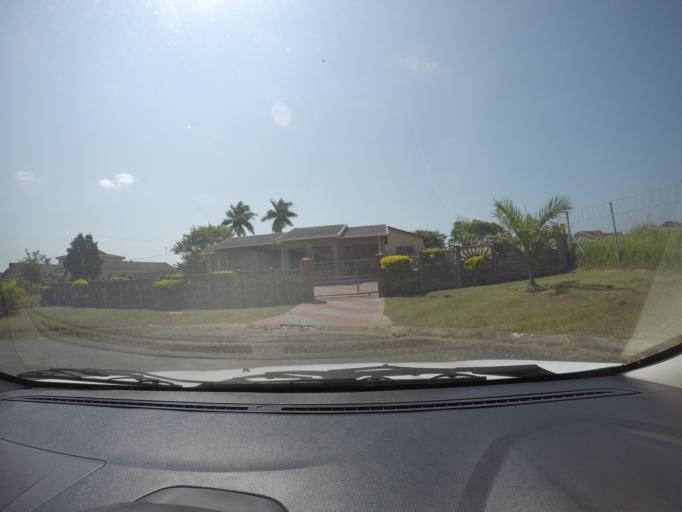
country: ZA
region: KwaZulu-Natal
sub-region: uThungulu District Municipality
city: eSikhawini
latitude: -28.8685
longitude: 31.9123
